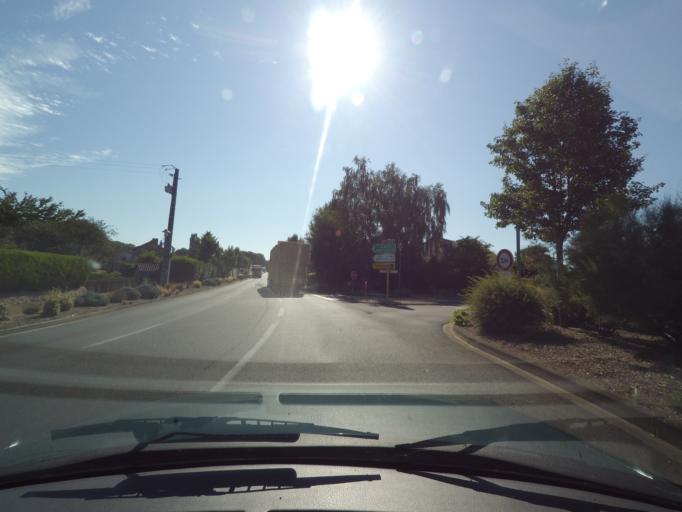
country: FR
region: Poitou-Charentes
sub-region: Departement de la Vienne
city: Lussac-les-Chateaux
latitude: 46.4049
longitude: 0.6966
